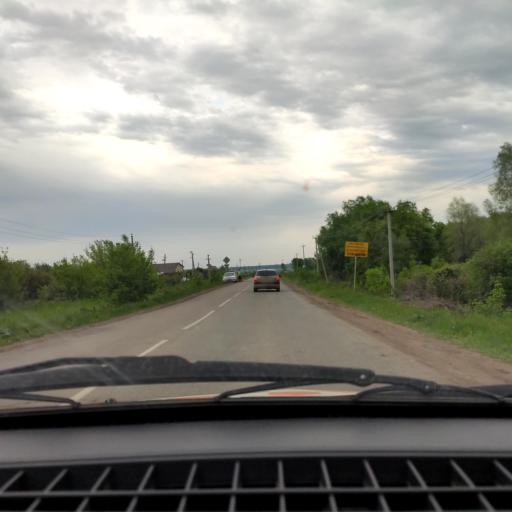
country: RU
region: Bashkortostan
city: Avdon
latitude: 54.5795
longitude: 55.7513
